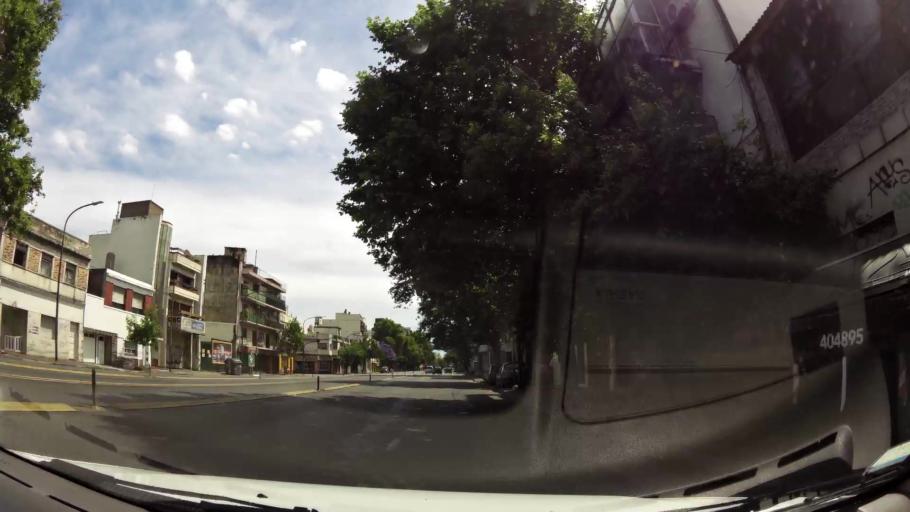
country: AR
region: Buenos Aires F.D.
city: Villa Santa Rita
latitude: -34.6243
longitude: -58.4840
